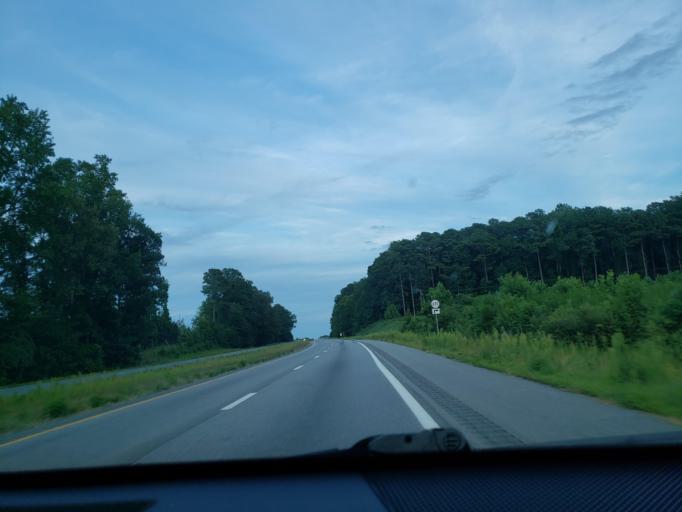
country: US
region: Virginia
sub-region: Southampton County
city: Courtland
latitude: 36.7036
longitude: -77.2729
